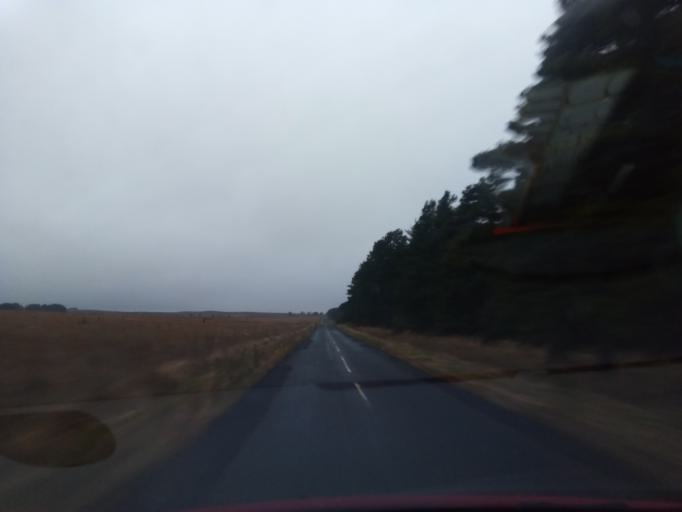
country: GB
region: England
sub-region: Northumberland
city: Rothley
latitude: 55.2047
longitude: -2.0137
